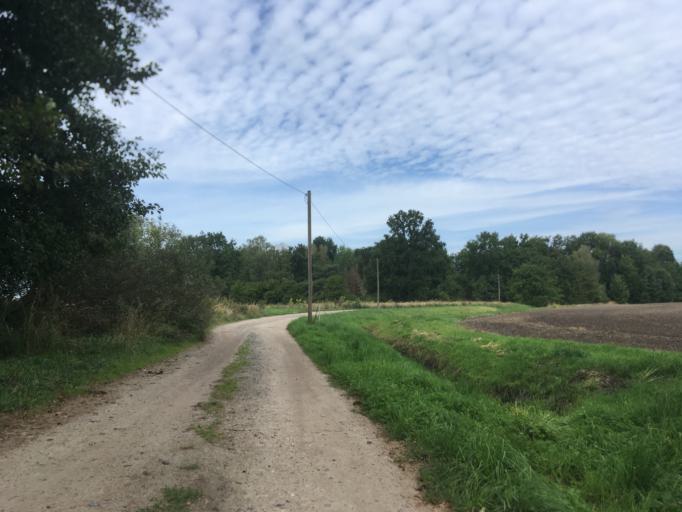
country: DE
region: Brandenburg
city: Wandlitz
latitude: 52.7561
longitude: 13.4150
